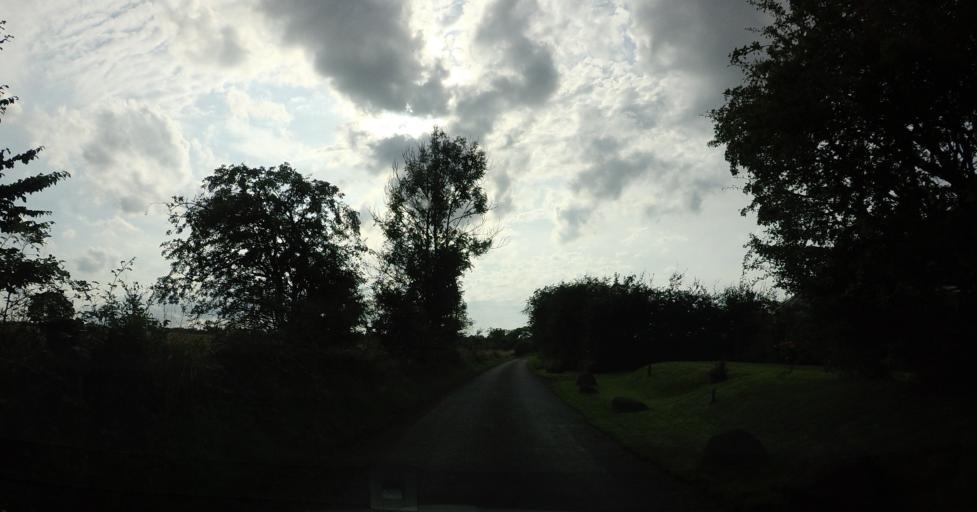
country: GB
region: Scotland
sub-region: Perth and Kinross
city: Auchterarder
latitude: 56.3009
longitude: -3.7540
